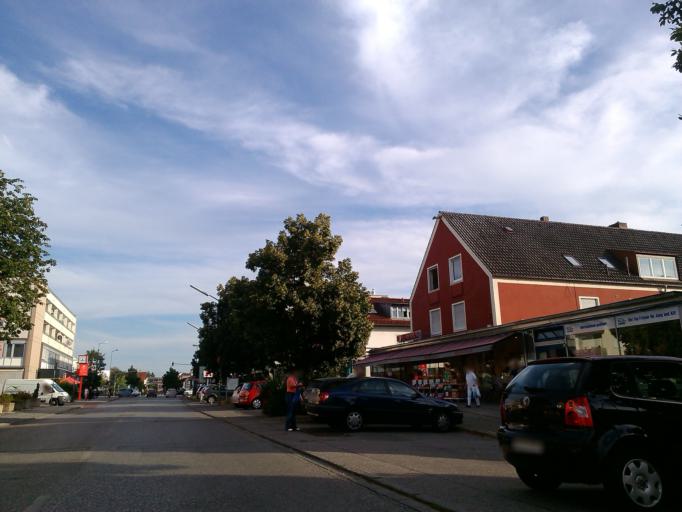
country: DE
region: Bavaria
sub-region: Upper Bavaria
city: Germering
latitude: 48.1320
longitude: 11.3643
